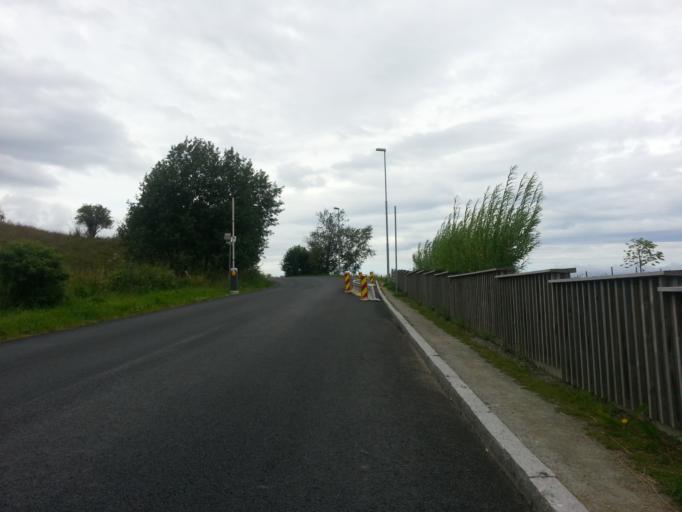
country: NO
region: Sor-Trondelag
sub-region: Trondheim
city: Trondheim
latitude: 63.4347
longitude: 10.4884
